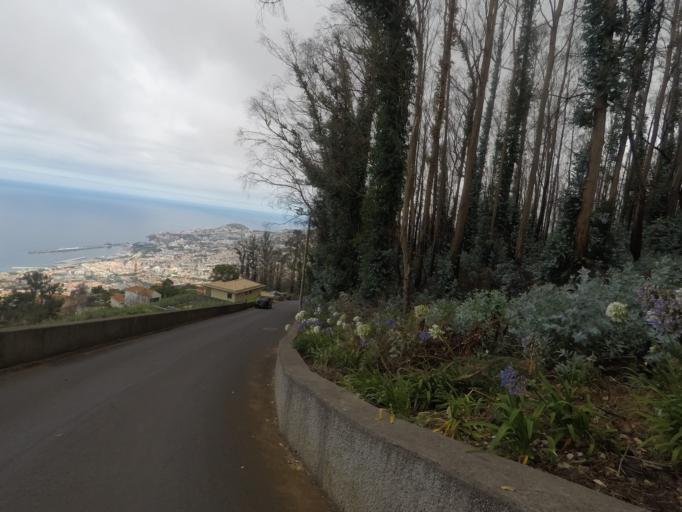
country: PT
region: Madeira
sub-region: Funchal
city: Nossa Senhora do Monte
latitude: 32.6669
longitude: -16.8845
